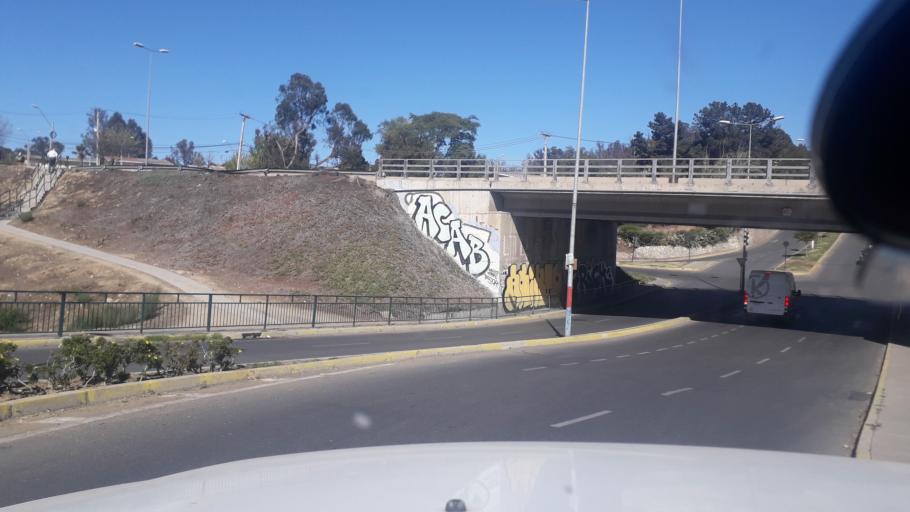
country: CL
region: Valparaiso
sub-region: Provincia de Valparaiso
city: Vina del Mar
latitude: -33.0373
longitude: -71.5073
